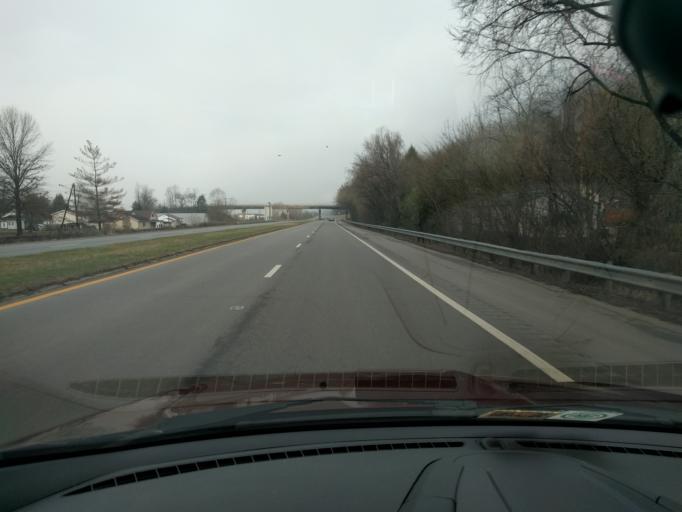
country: US
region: West Virginia
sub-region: Kanawha County
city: Chesapeake
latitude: 38.2233
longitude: -81.5268
